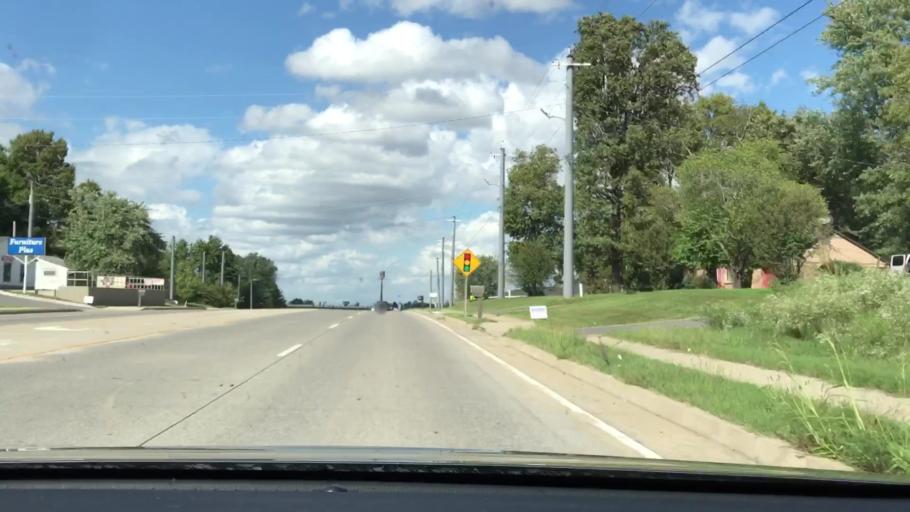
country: US
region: Kentucky
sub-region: Graves County
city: Mayfield
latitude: 36.7634
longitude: -88.6427
